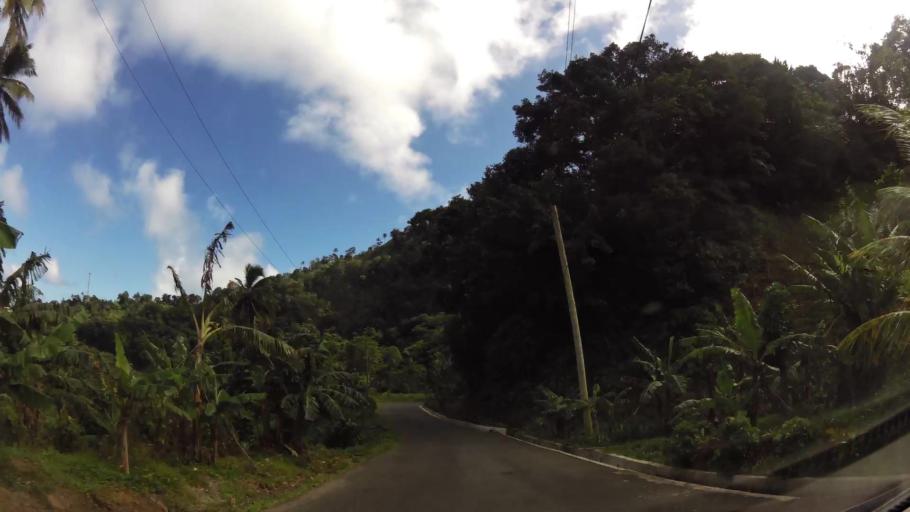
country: DM
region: Saint John
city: Portsmouth
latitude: 15.6267
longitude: -61.4283
